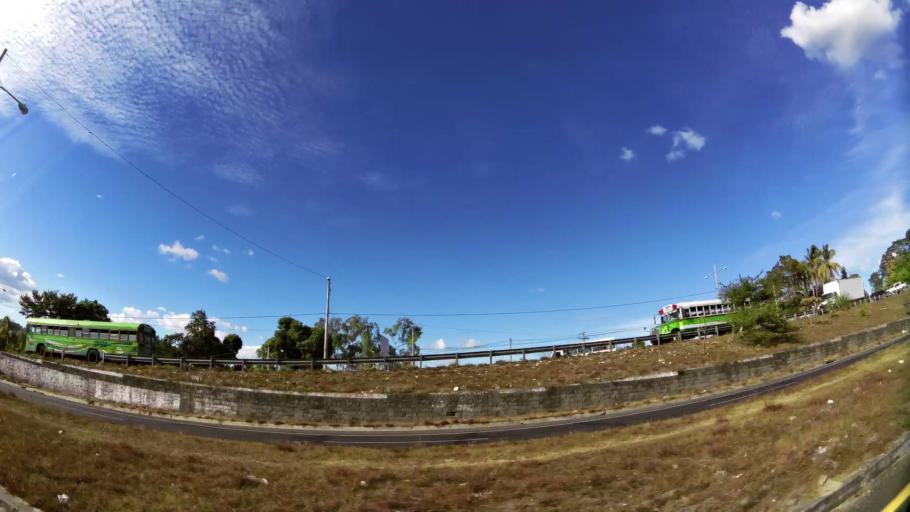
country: SV
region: San Salvador
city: Ilopango
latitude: 13.7360
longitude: -89.0498
